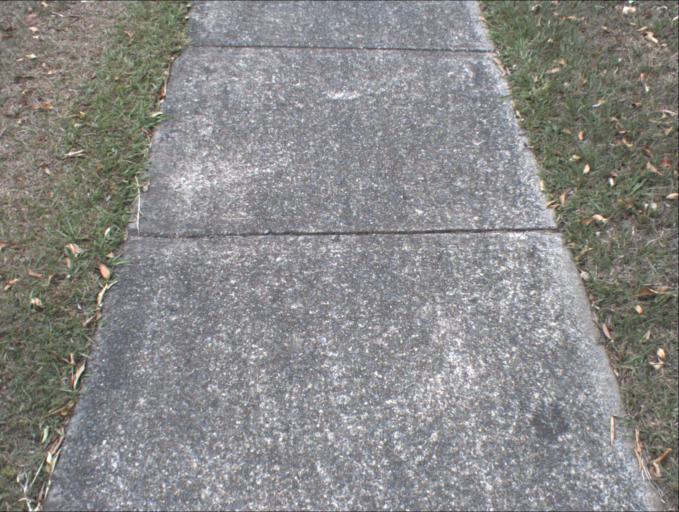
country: AU
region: Queensland
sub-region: Logan
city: Springwood
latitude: -27.6263
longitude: 153.1279
